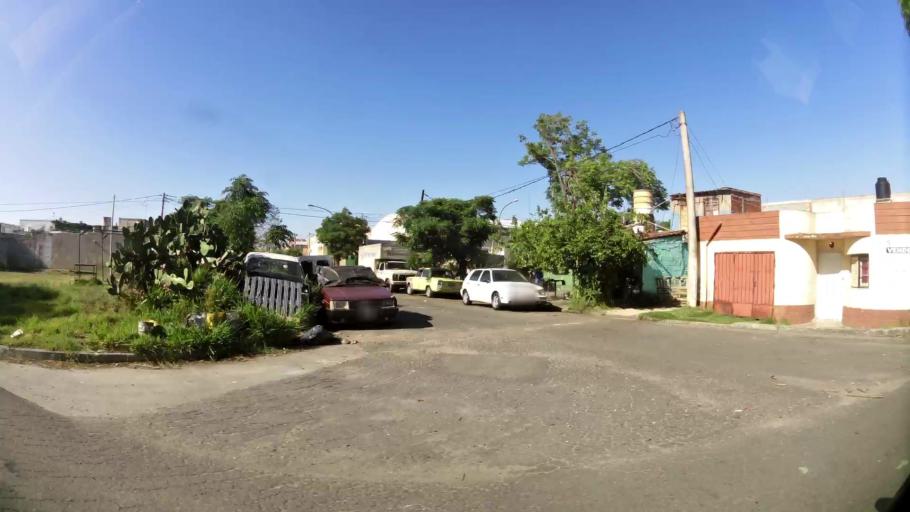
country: AR
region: Cordoba
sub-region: Departamento de Capital
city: Cordoba
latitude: -31.4170
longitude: -64.1548
